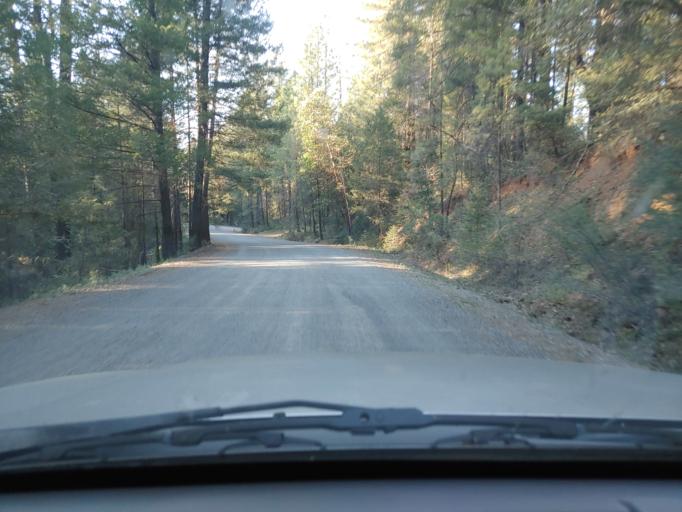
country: US
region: California
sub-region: Shasta County
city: Bella Vista
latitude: 40.8240
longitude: -122.0179
